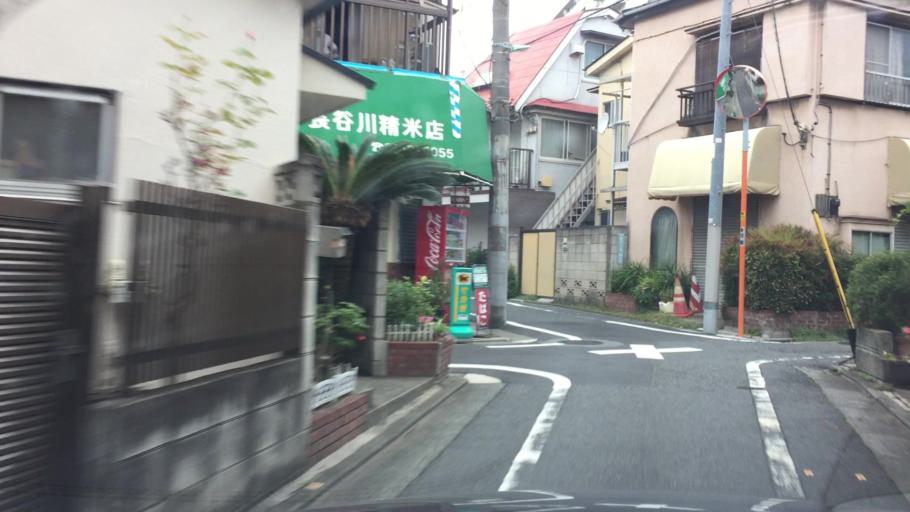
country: JP
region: Tokyo
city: Tokyo
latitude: 35.6453
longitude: 139.6890
